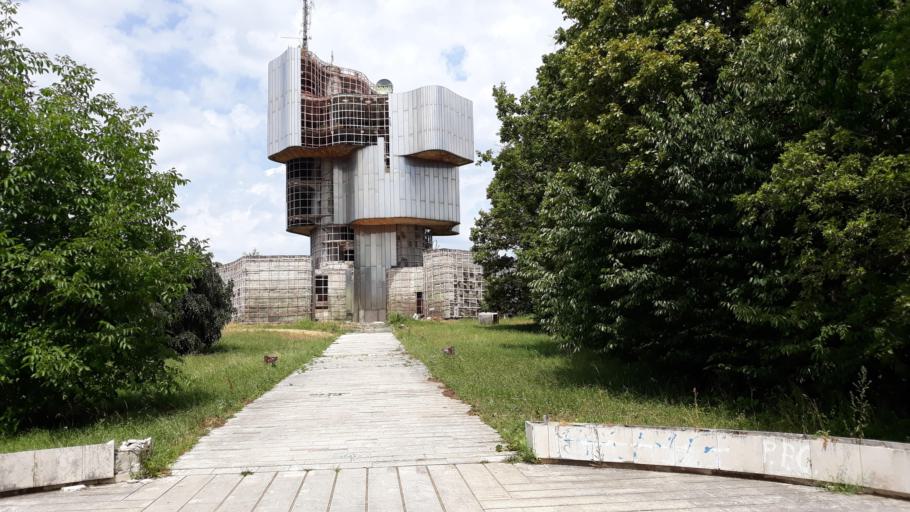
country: HR
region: Sisacko-Moslavacka
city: Gvozd
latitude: 45.3153
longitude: 15.8051
